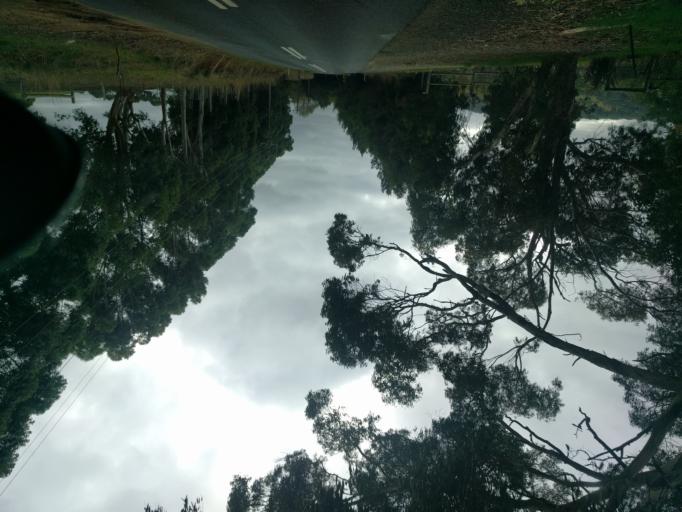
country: AU
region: South Australia
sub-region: Adelaide Hills
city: Stirling
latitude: -35.0603
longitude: 138.7621
